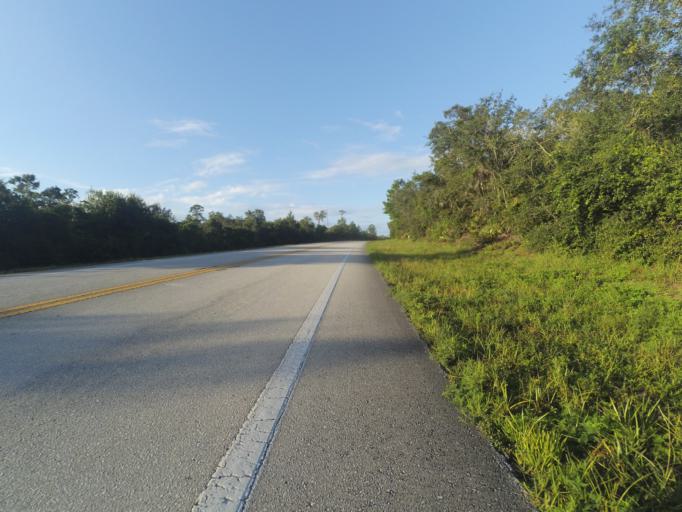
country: US
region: Florida
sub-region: Lake County
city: Astor
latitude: 29.2197
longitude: -81.6464
